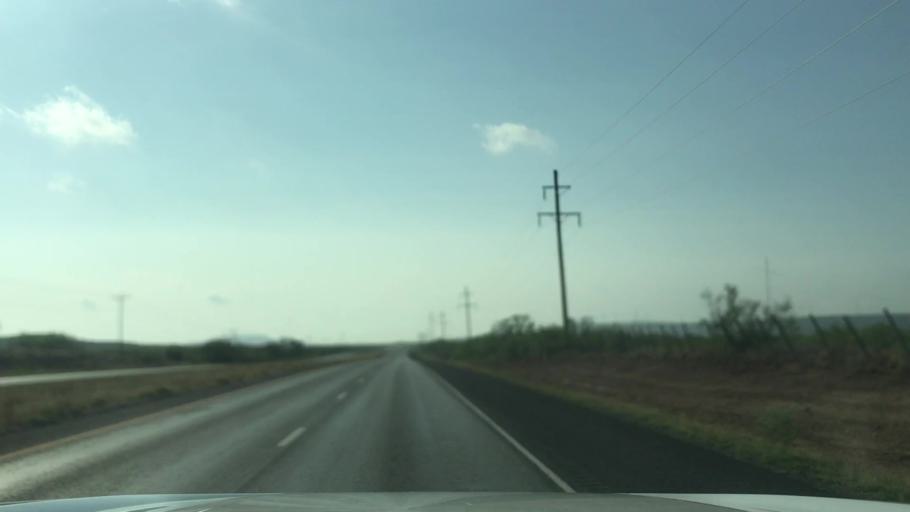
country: US
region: Texas
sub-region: Garza County
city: Post
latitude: 33.0001
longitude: -101.1587
